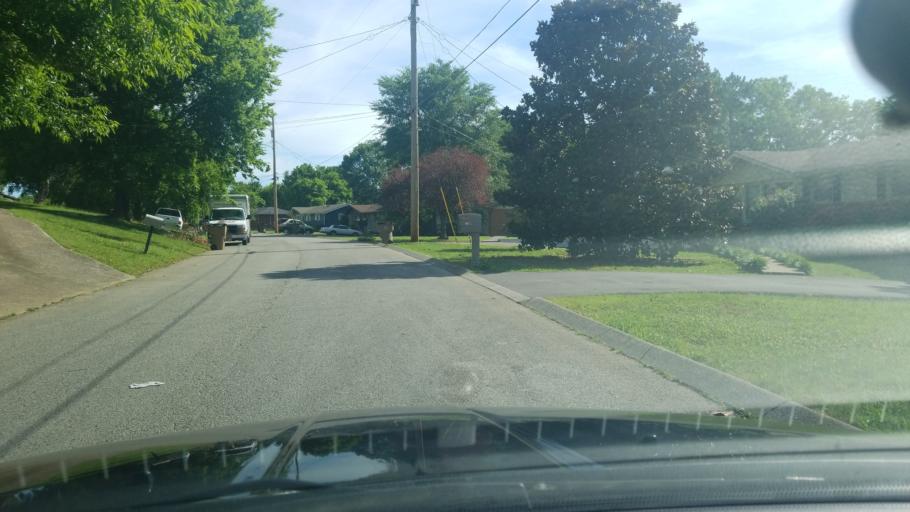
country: US
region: Tennessee
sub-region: Davidson County
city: Nashville
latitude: 36.2367
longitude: -86.7769
